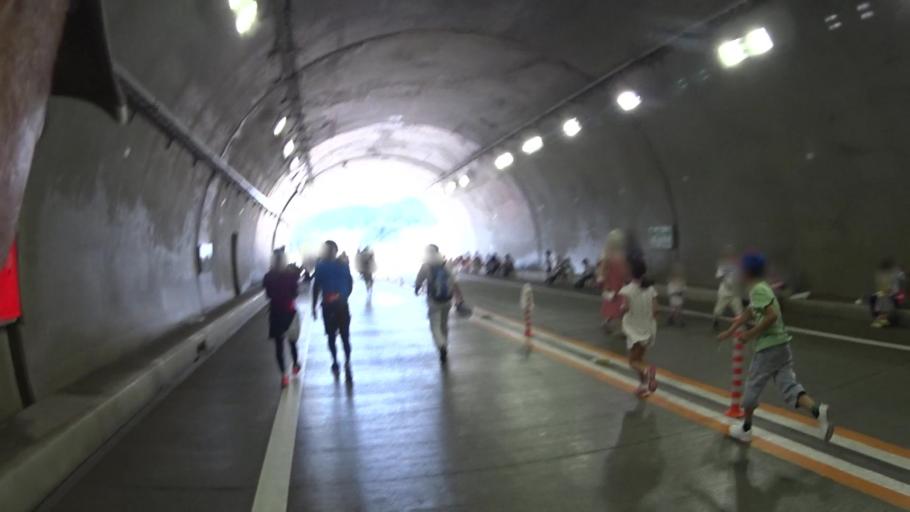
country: JP
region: Hyogo
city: Sasayama
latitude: 35.1585
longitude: 135.4057
